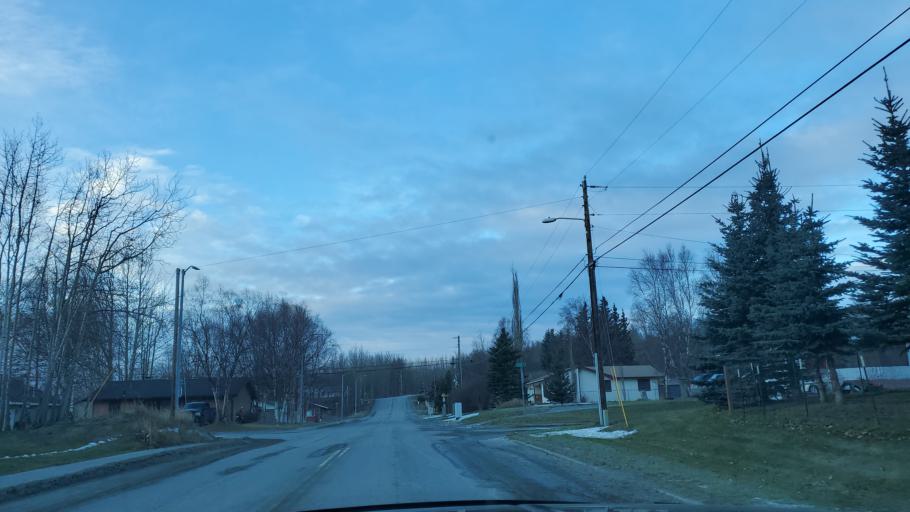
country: US
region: Alaska
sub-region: Matanuska-Susitna Borough
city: Palmer
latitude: 61.6139
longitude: -149.1137
